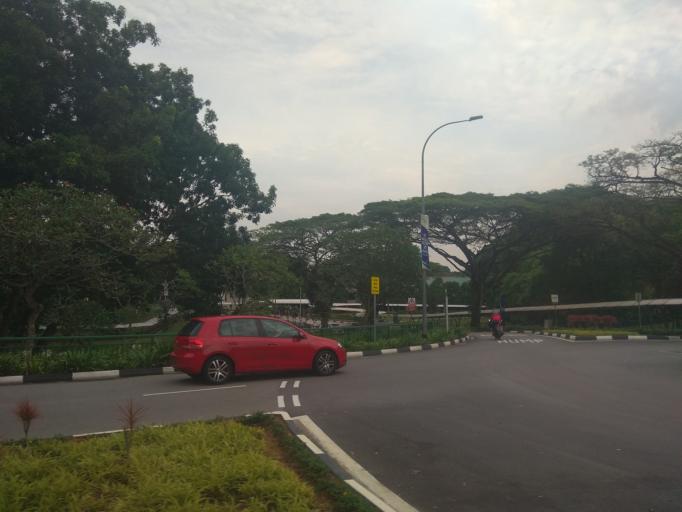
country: MY
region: Johor
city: Johor Bahru
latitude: 1.3497
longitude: 103.6851
